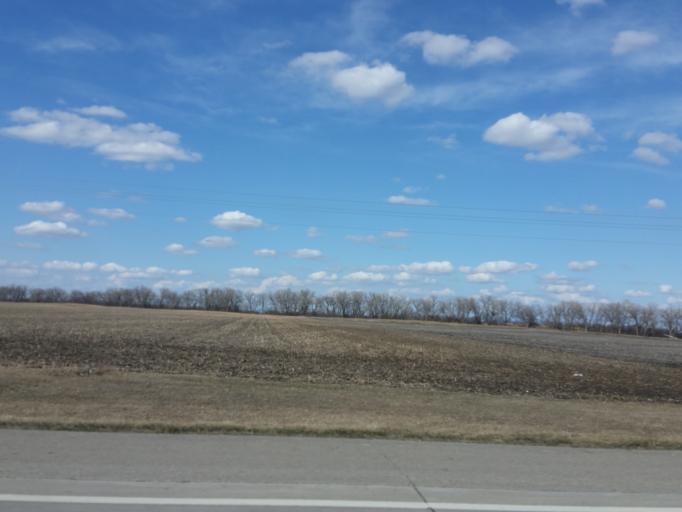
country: US
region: Minnesota
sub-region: Lac qui Parle County
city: Dawson
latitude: 44.9356
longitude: -96.0743
